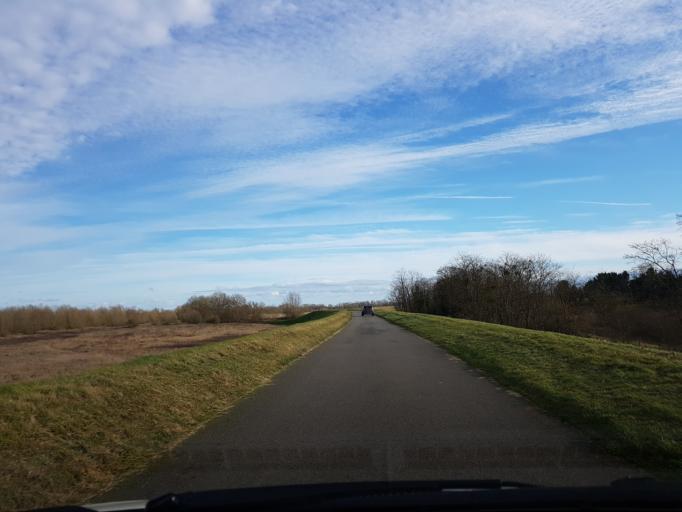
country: FR
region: Centre
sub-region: Departement du Loiret
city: Checy
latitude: 47.8845
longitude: 2.0065
